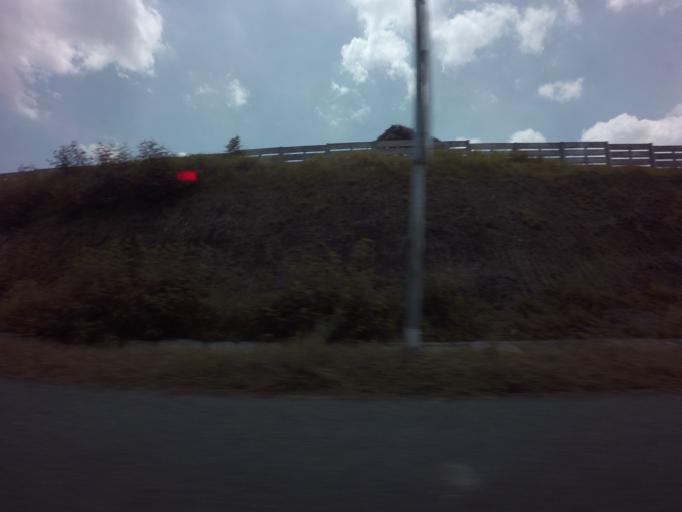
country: PH
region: Calabarzon
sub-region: Province of Laguna
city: San Pedro
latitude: 14.3771
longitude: 121.0206
